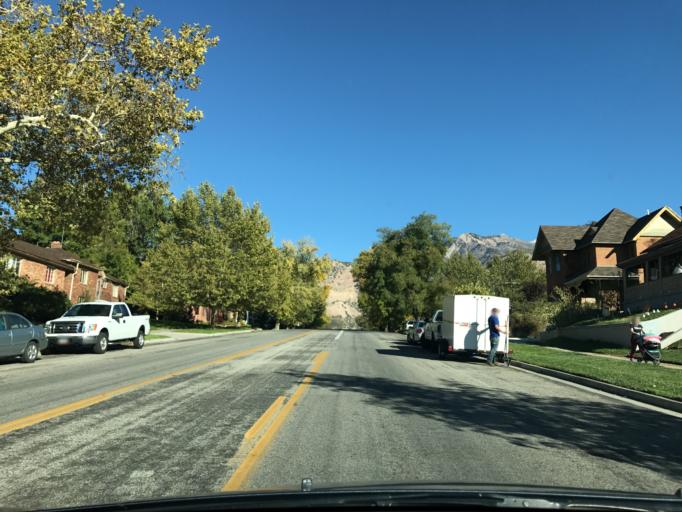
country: US
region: Utah
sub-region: Weber County
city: Ogden
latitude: 41.2185
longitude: -111.9661
